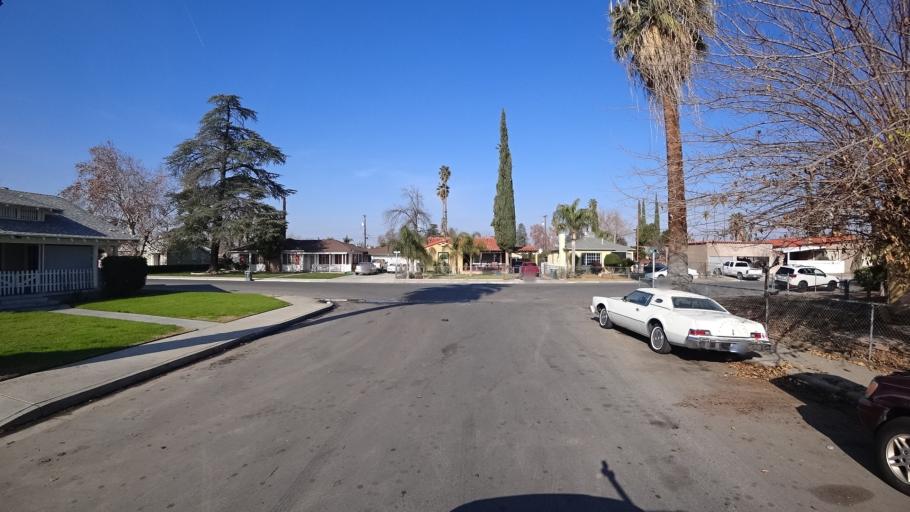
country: US
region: California
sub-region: Kern County
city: Bakersfield
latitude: 35.3651
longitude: -119.0051
